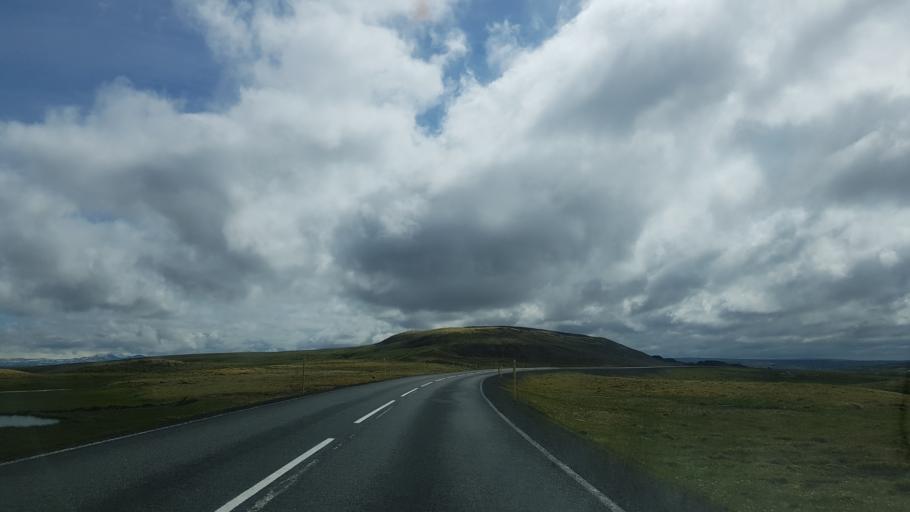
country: IS
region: West
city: Borgarnes
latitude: 64.9879
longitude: -21.0553
